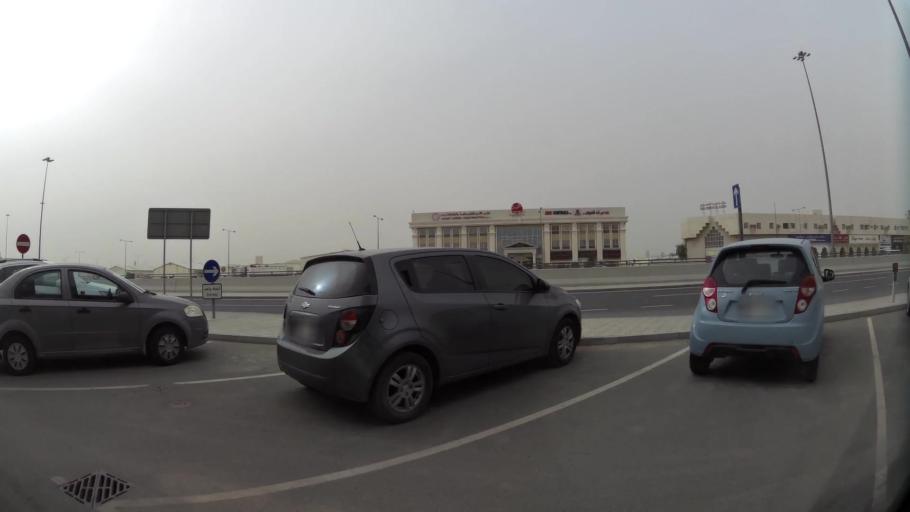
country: QA
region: Baladiyat ad Dawhah
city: Doha
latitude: 25.2574
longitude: 51.4866
